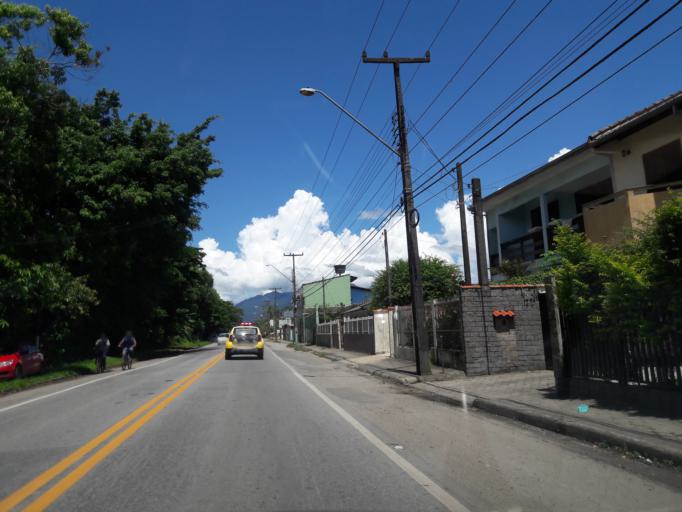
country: BR
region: Parana
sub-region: Antonina
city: Antonina
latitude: -25.4837
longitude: -48.8285
